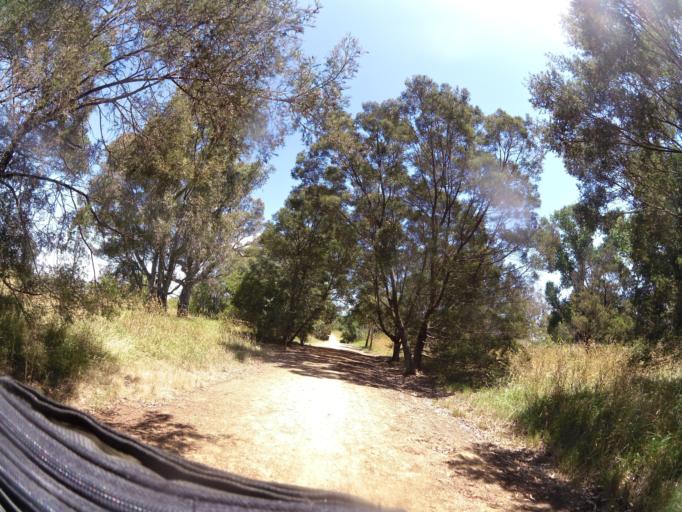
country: AU
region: Victoria
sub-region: Wellington
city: Heyfield
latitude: -37.9697
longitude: 146.9500
